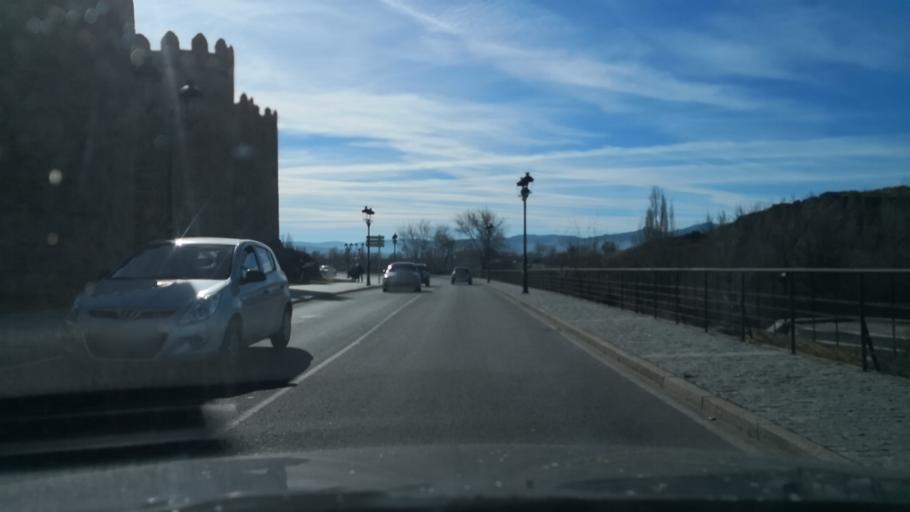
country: ES
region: Castille and Leon
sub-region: Provincia de Avila
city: Avila
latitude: 40.6572
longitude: -4.7075
